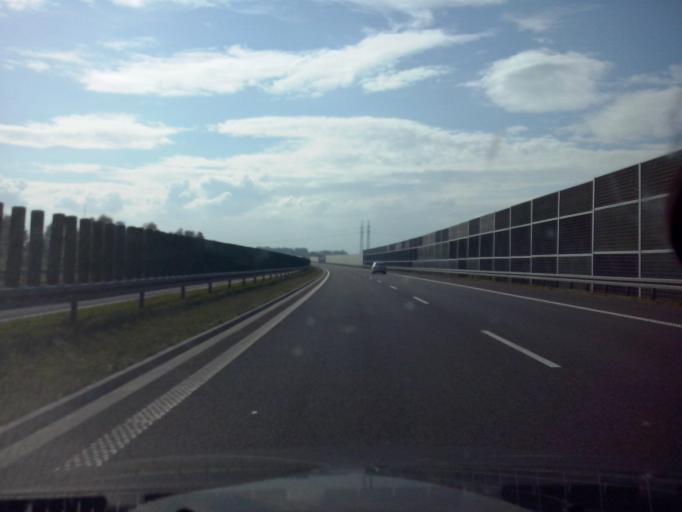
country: PL
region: Lesser Poland Voivodeship
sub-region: Powiat tarnowski
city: Lukowa
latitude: 50.0580
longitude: 20.9305
